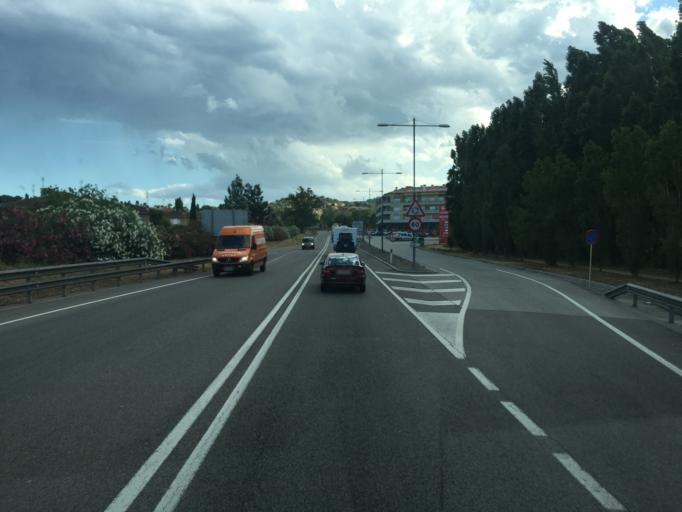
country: ES
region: Catalonia
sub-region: Provincia de Barcelona
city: Tordera
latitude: 41.6950
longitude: 2.7249
